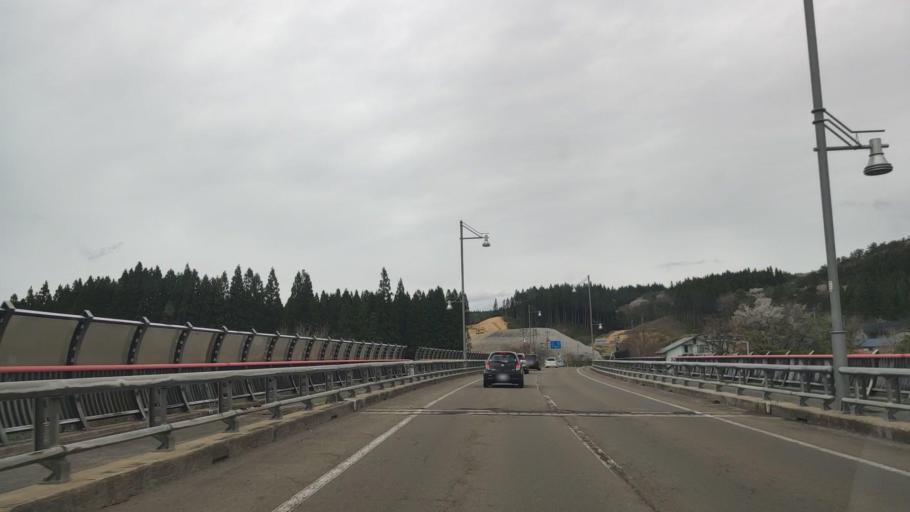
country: JP
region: Akita
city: Takanosu
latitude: 40.2108
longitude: 140.3018
